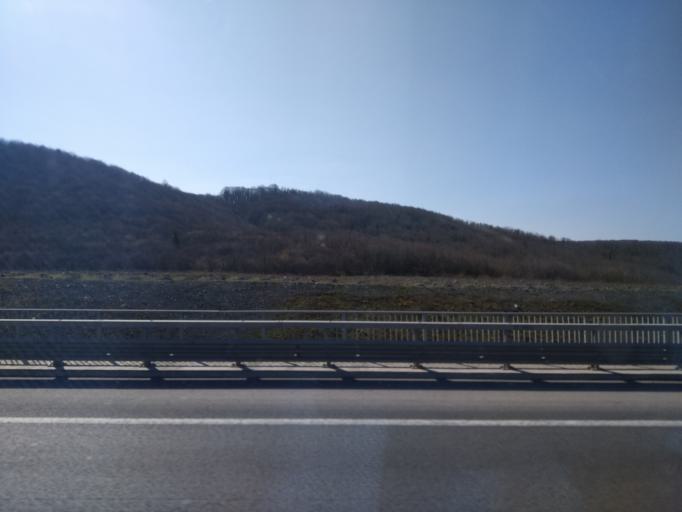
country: TR
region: Istanbul
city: Mahmut Sevket Pasa
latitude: 41.1506
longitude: 29.2705
